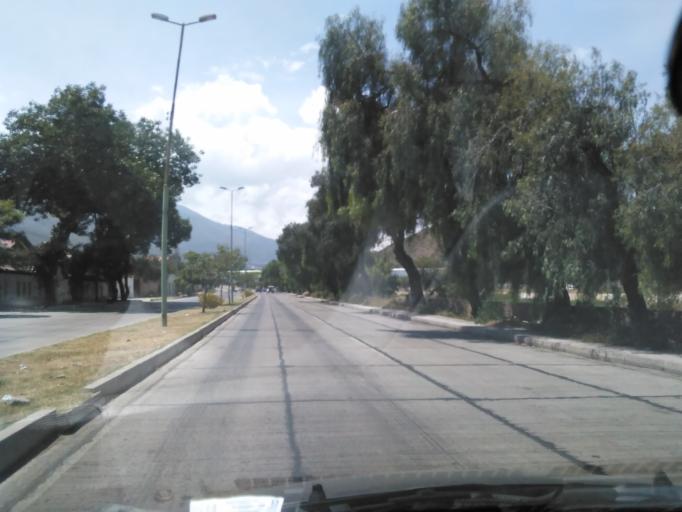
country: BO
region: Cochabamba
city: Cochabamba
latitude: -17.3763
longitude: -66.1405
